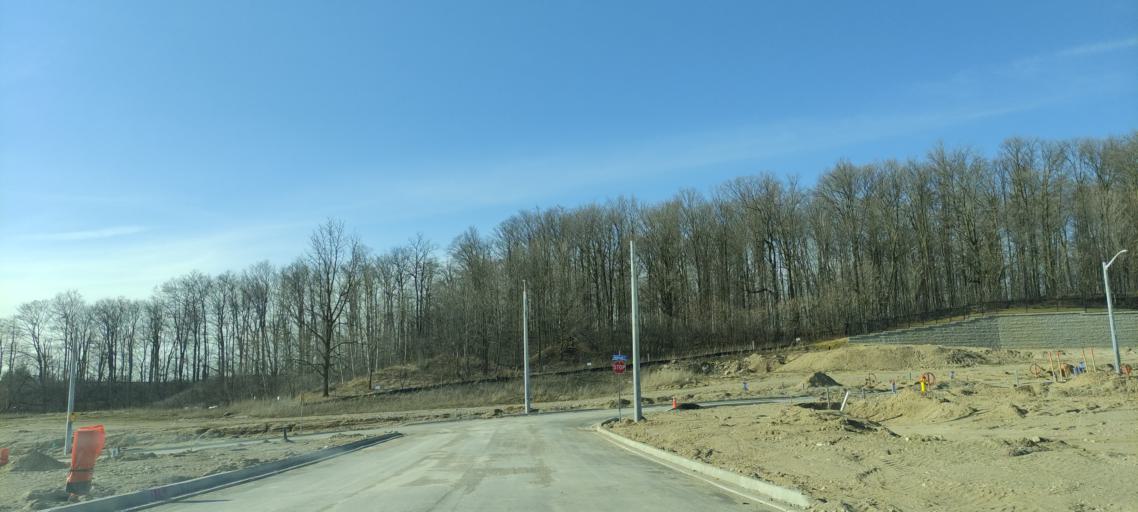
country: CA
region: Ontario
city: Kitchener
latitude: 43.4037
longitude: -80.5379
